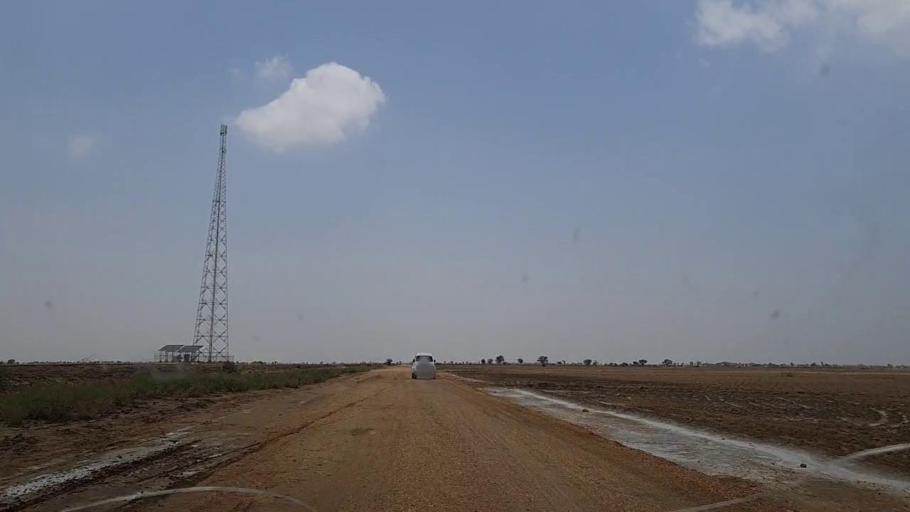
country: PK
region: Sindh
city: Johi
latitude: 26.7868
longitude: 67.6457
